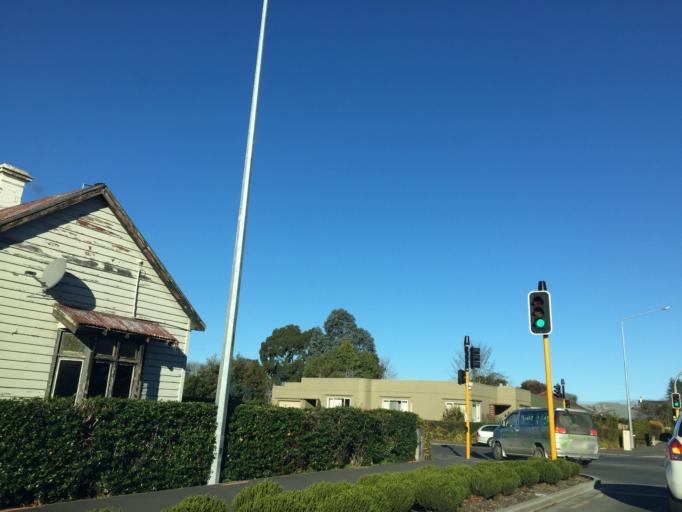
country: NZ
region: Southland
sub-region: Invercargill City
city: Invercargill
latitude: -46.4036
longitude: 168.3615
